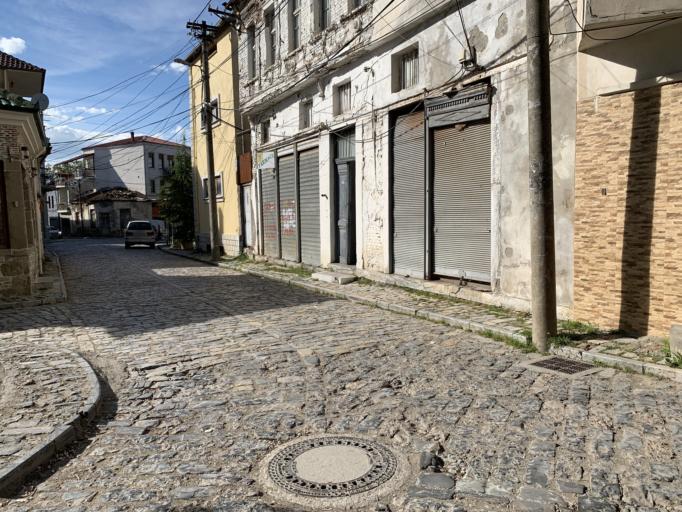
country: AL
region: Korce
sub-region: Rrethi i Korces
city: Korce
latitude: 40.6152
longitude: 20.7833
